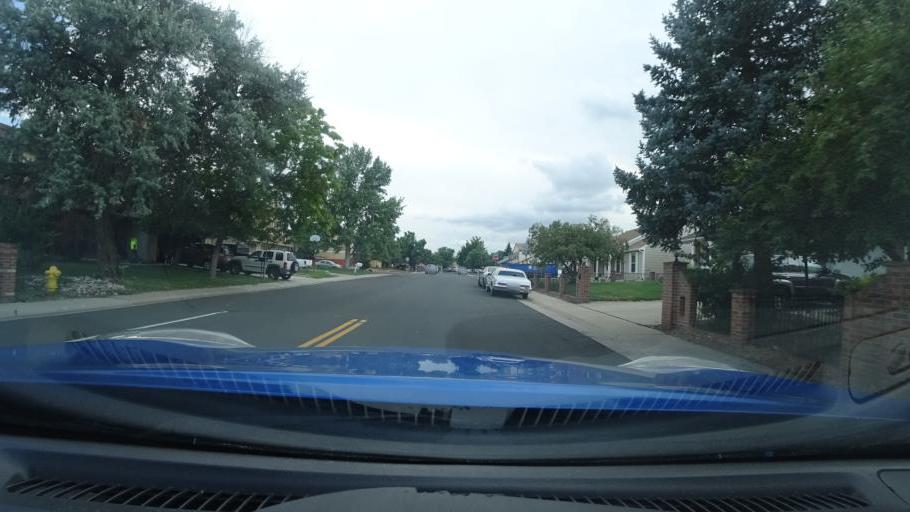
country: US
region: Colorado
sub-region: Adams County
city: Aurora
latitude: 39.6963
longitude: -104.8028
